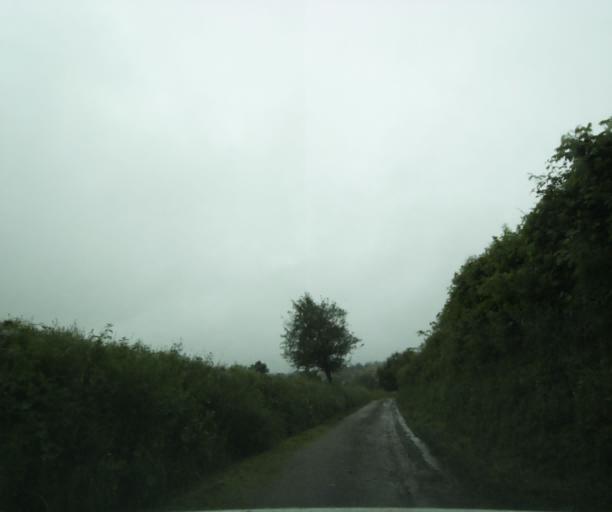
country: FR
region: Bourgogne
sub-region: Departement de Saone-et-Loire
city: Charolles
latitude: 46.4057
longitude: 4.3870
